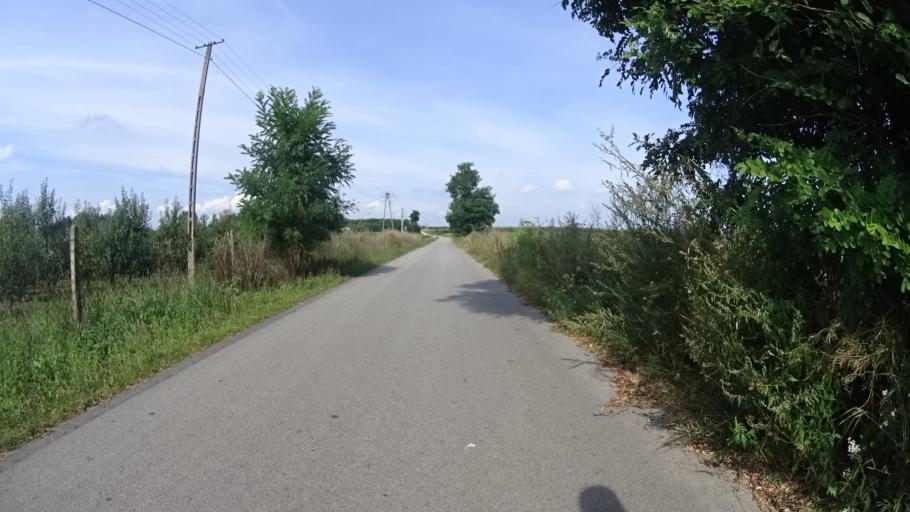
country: PL
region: Masovian Voivodeship
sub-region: Powiat grojecki
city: Goszczyn
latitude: 51.6822
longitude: 20.8403
